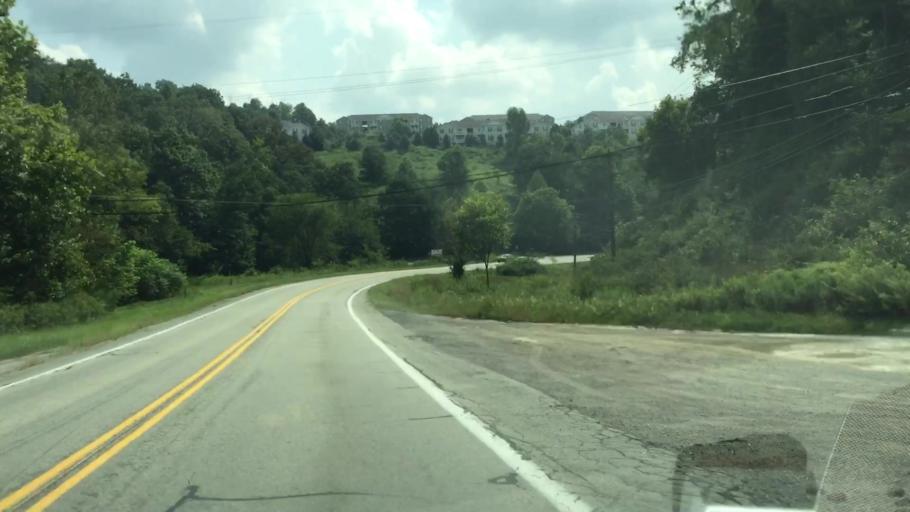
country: US
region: Pennsylvania
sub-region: Allegheny County
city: Coraopolis
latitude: 40.4661
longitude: -80.1543
